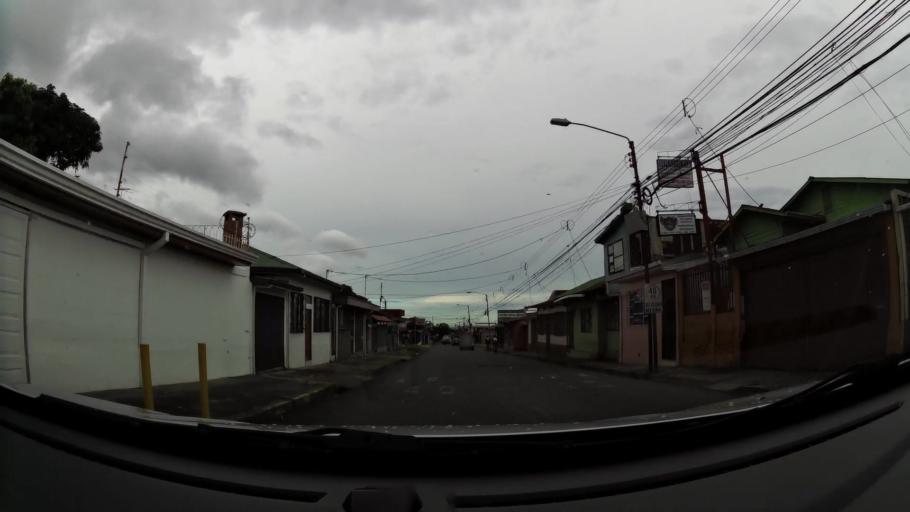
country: CR
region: San Jose
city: San Juan
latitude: 9.9633
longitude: -84.0811
